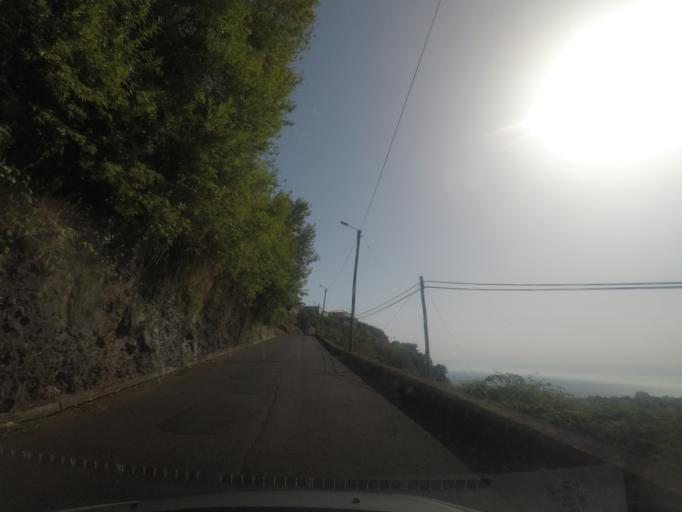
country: PT
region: Madeira
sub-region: Calheta
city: Arco da Calheta
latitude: 32.7284
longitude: -17.1652
